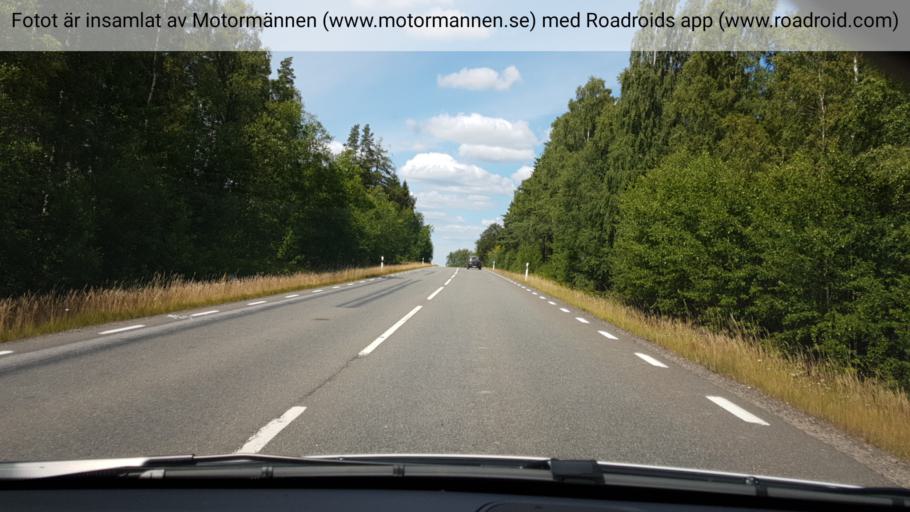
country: SE
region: Vaestra Goetaland
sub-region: Toreboda Kommun
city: Toereboda
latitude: 58.5659
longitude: 14.1116
